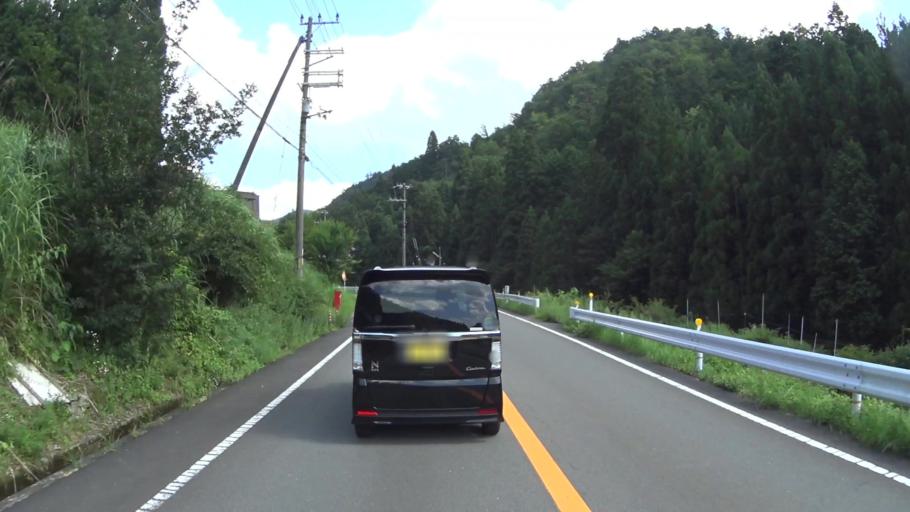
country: JP
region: Kyoto
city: Kameoka
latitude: 35.2646
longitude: 135.6016
